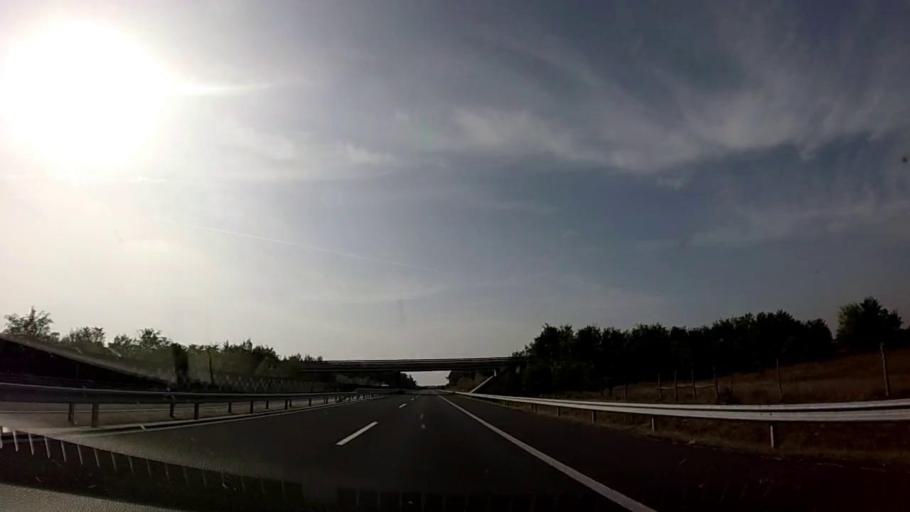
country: HU
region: Somogy
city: Balatonbereny
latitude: 46.6374
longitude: 17.2835
